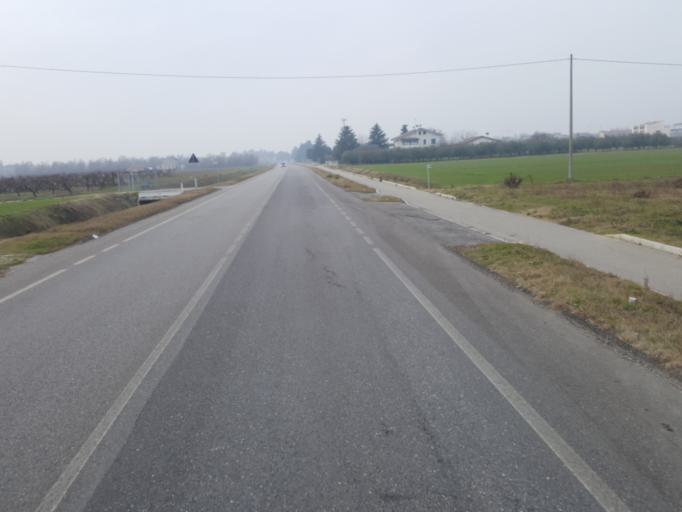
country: IT
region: Emilia-Romagna
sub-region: Forli-Cesena
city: Cesena
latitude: 44.1564
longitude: 12.2825
